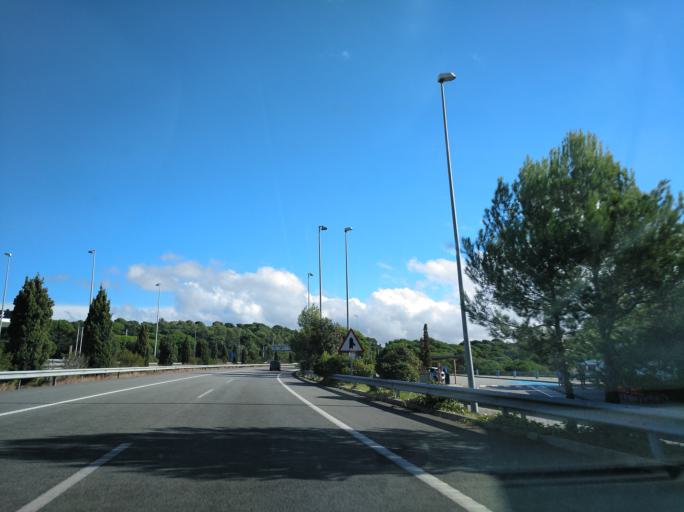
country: ES
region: Catalonia
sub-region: Provincia de Barcelona
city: Tordera
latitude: 41.6684
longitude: 2.7157
